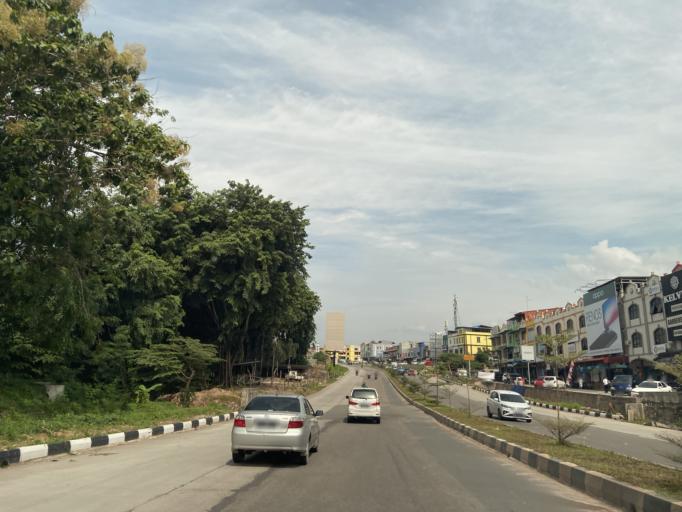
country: SG
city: Singapore
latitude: 1.1221
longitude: 104.0333
